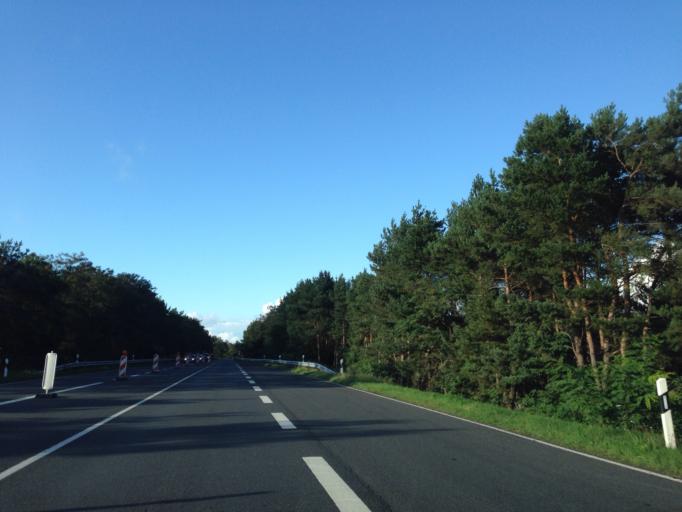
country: DE
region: Lower Saxony
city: Wendisch Evern
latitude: 53.2405
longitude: 10.4734
